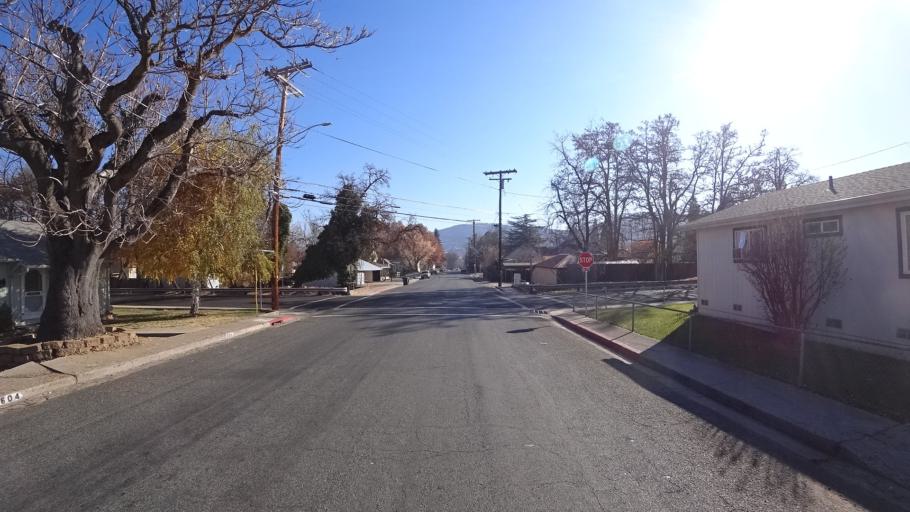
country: US
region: California
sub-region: Siskiyou County
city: Yreka
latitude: 41.7345
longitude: -122.6401
